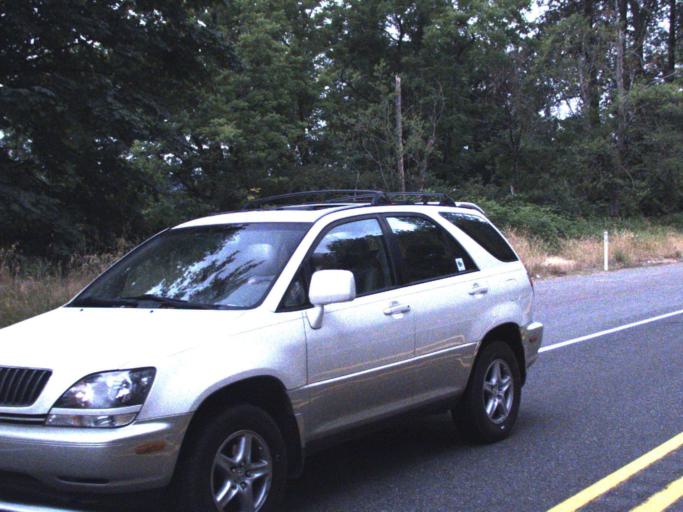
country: US
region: Washington
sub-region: King County
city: Duvall
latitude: 47.7799
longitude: -121.9641
